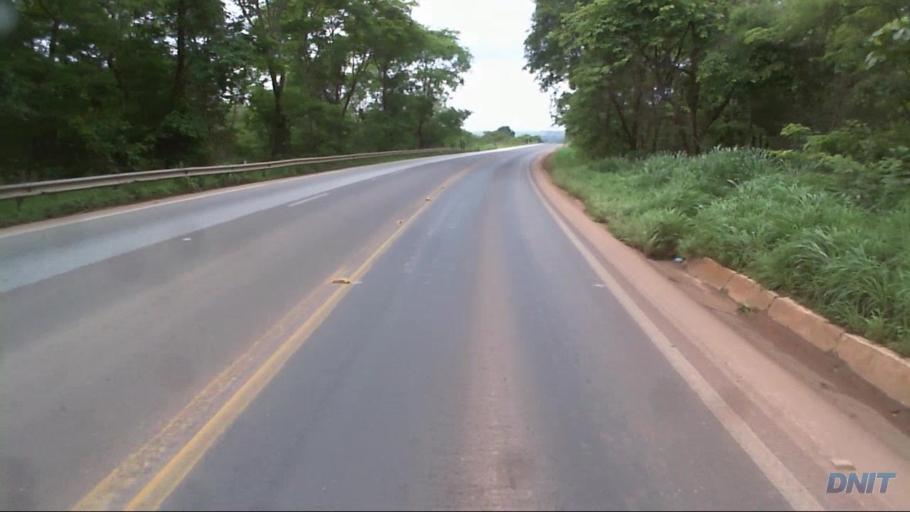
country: BR
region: Goias
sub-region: Uruacu
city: Uruacu
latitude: -14.5708
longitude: -49.1564
